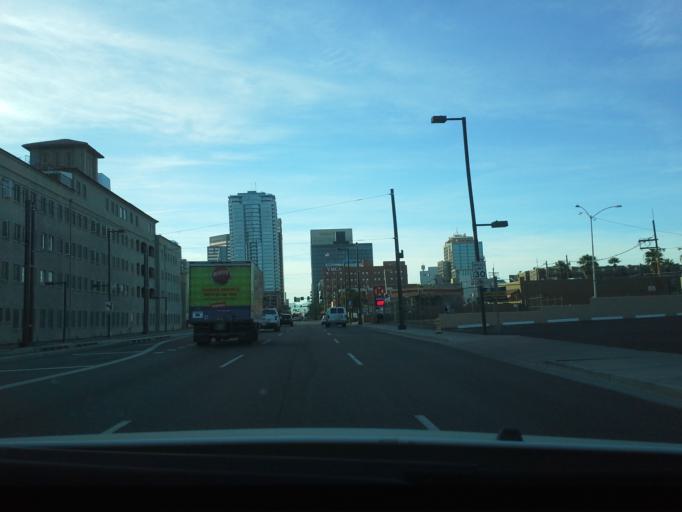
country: US
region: Arizona
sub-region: Maricopa County
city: Phoenix
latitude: 33.4561
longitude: -112.0752
